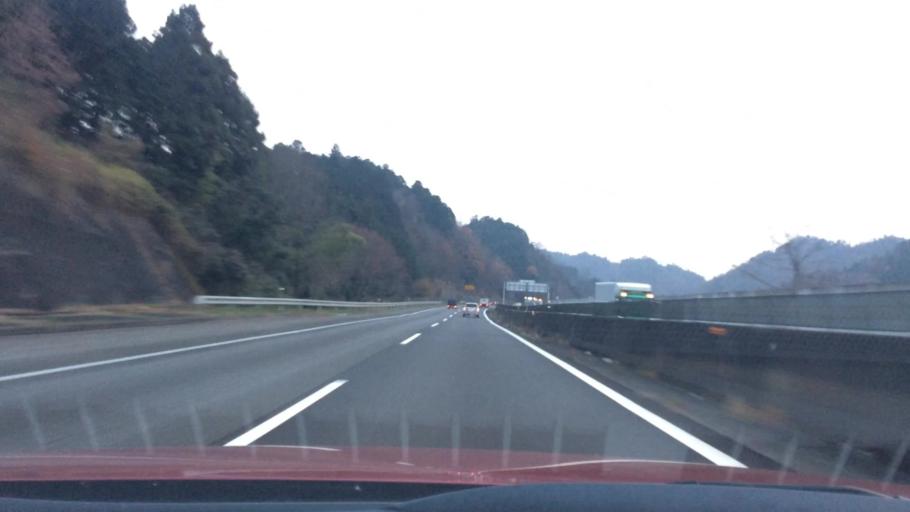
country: JP
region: Shiga Prefecture
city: Nagahama
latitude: 35.3105
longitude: 136.3138
